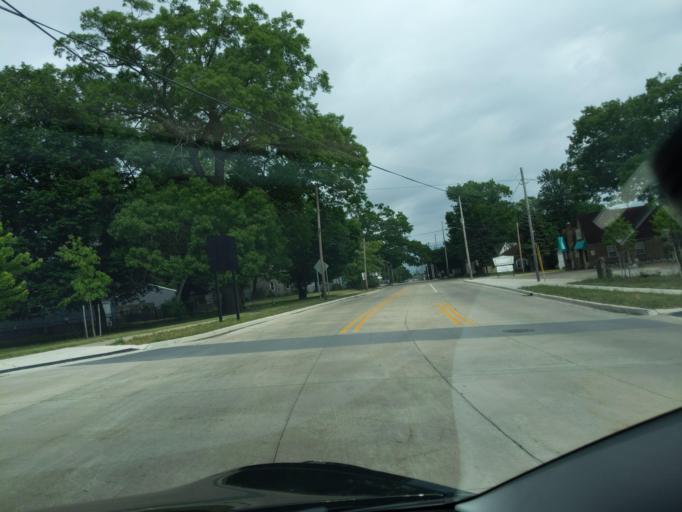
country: US
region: Michigan
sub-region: Muskegon County
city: Roosevelt Park
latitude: 43.2201
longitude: -86.2812
